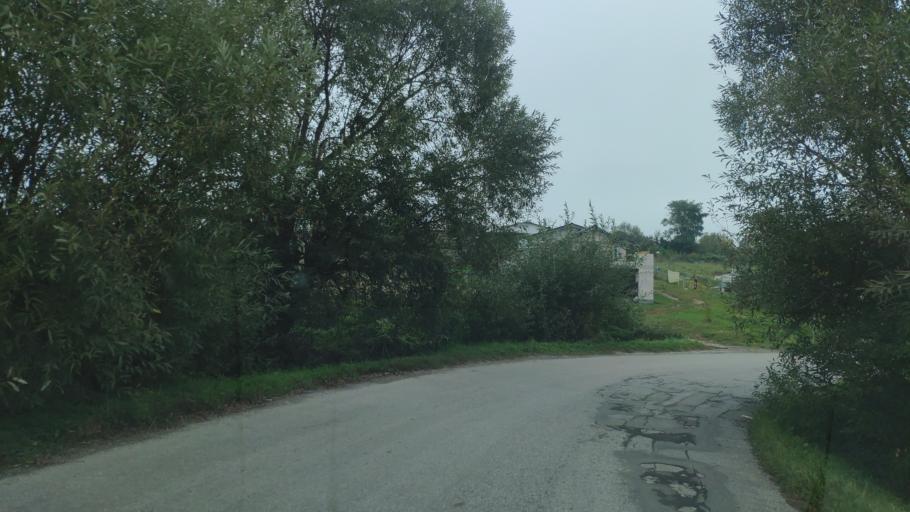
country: SK
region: Kosicky
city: Kosice
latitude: 48.8195
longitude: 21.4060
